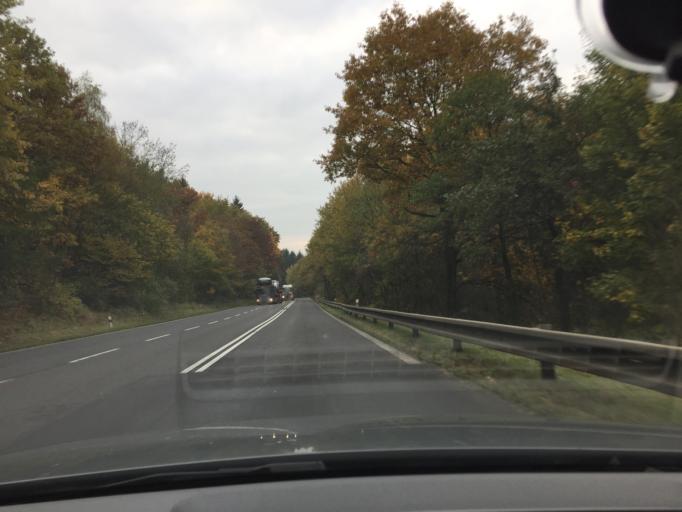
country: CZ
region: Ustecky
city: Rehlovice
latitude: 50.5710
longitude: 13.9539
